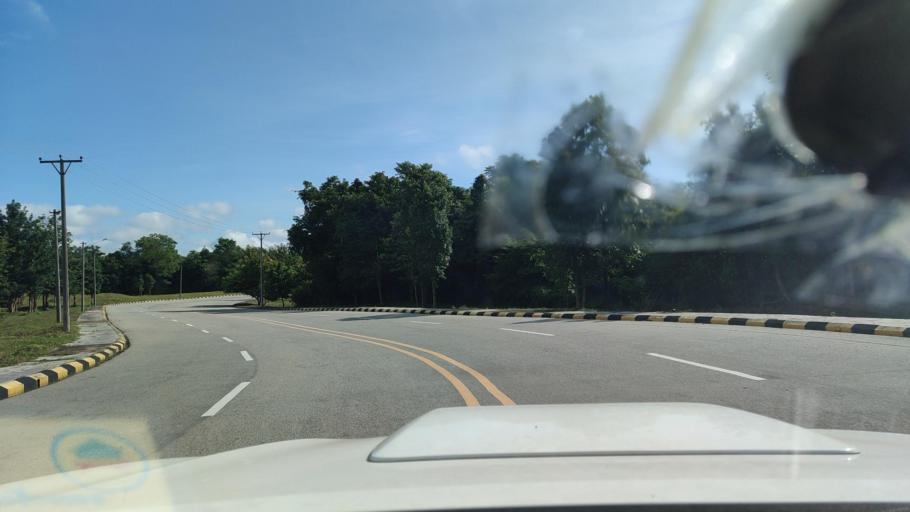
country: MM
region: Mandalay
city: Nay Pyi Taw
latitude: 19.8079
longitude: 96.1220
